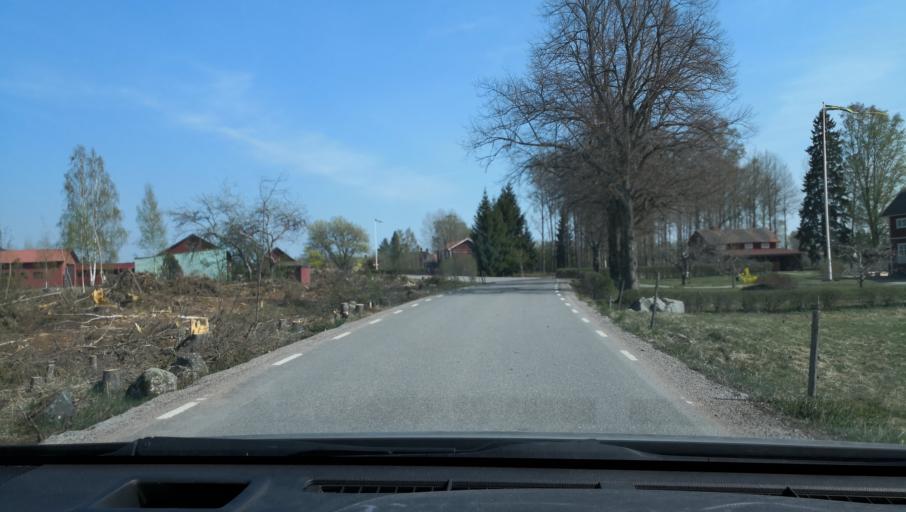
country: SE
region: Vaestmanland
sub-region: Sala Kommun
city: Sala
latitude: 60.0070
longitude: 16.6955
